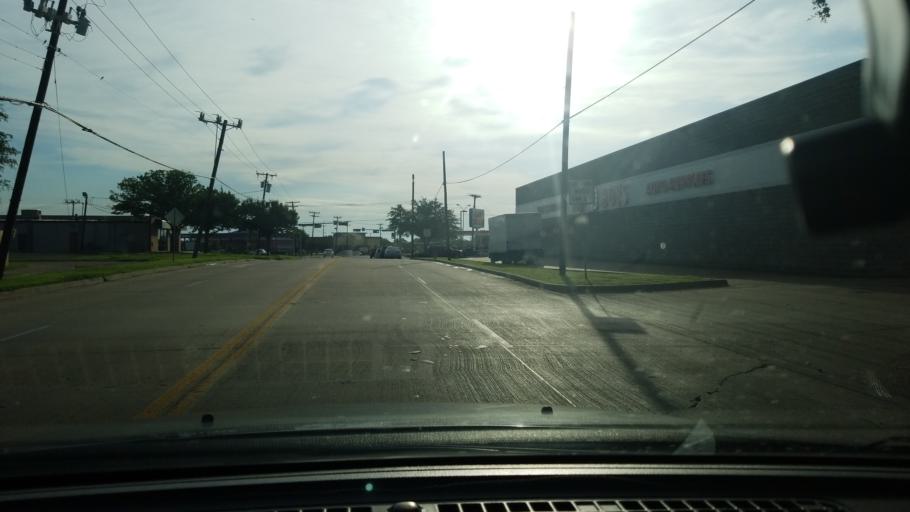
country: US
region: Texas
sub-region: Dallas County
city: Mesquite
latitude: 32.7966
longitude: -96.6131
